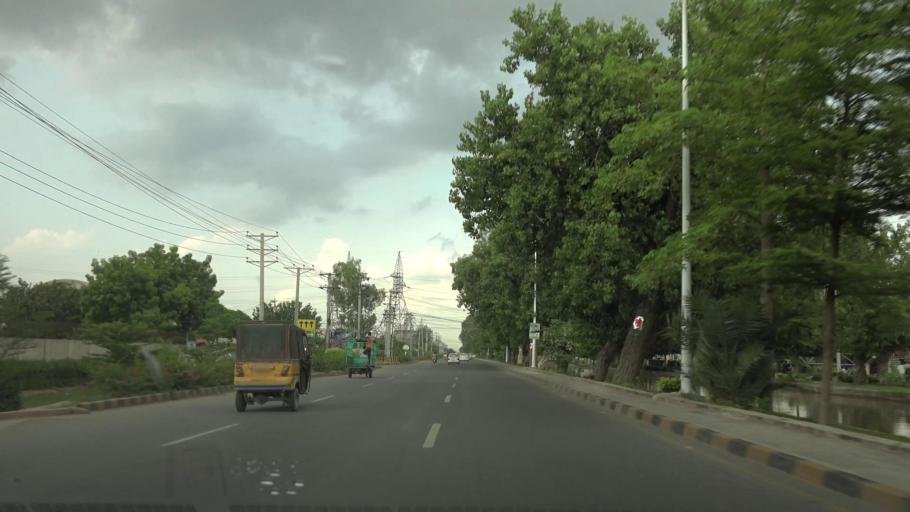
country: PK
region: Punjab
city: Faisalabad
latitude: 31.4309
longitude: 73.1209
